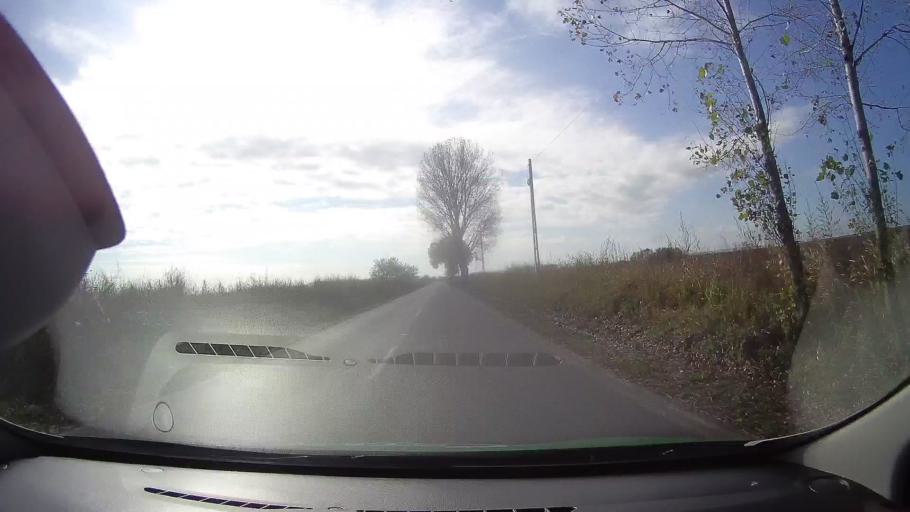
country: RO
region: Tulcea
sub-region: Comuna Valea Nucarilor
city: Agighiol
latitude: 44.9866
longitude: 28.8845
